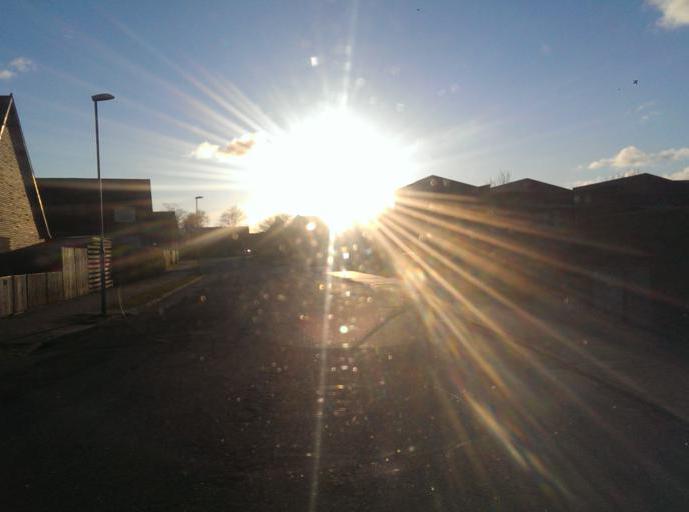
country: DK
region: South Denmark
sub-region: Esbjerg Kommune
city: Esbjerg
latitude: 55.4666
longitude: 8.4652
